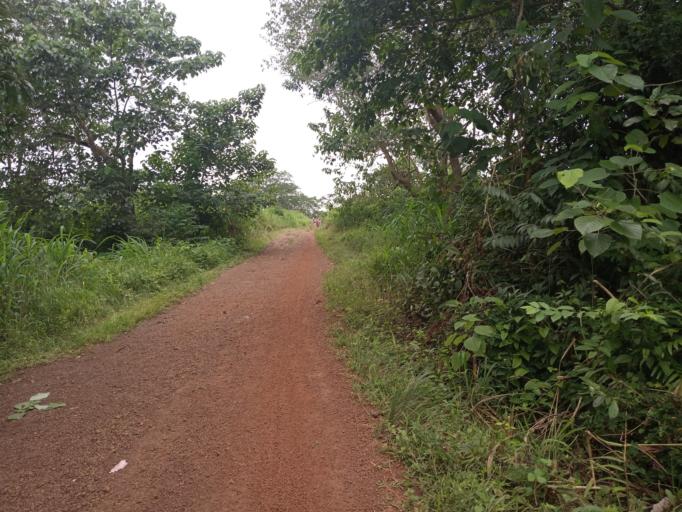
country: SL
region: Northern Province
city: Kamakwie
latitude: 9.4826
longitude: -12.2495
